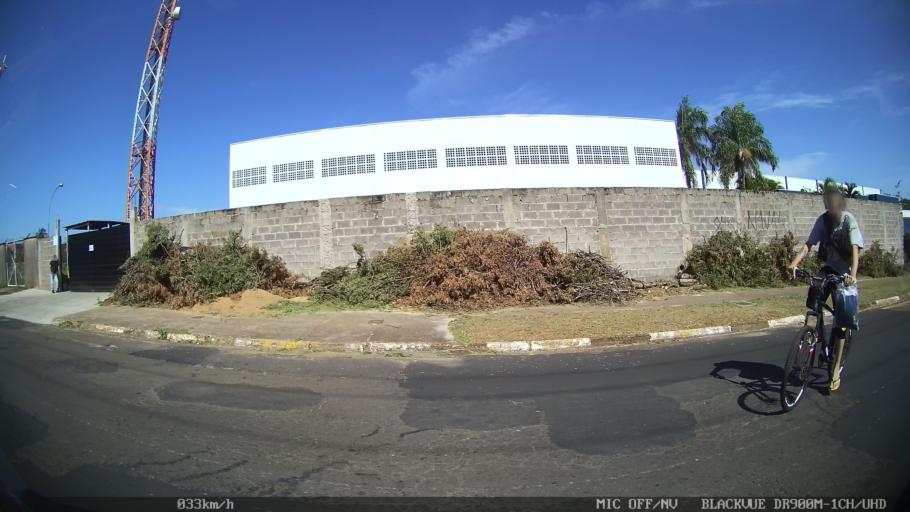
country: BR
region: Sao Paulo
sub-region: Franca
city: Franca
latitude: -20.5530
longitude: -47.4427
